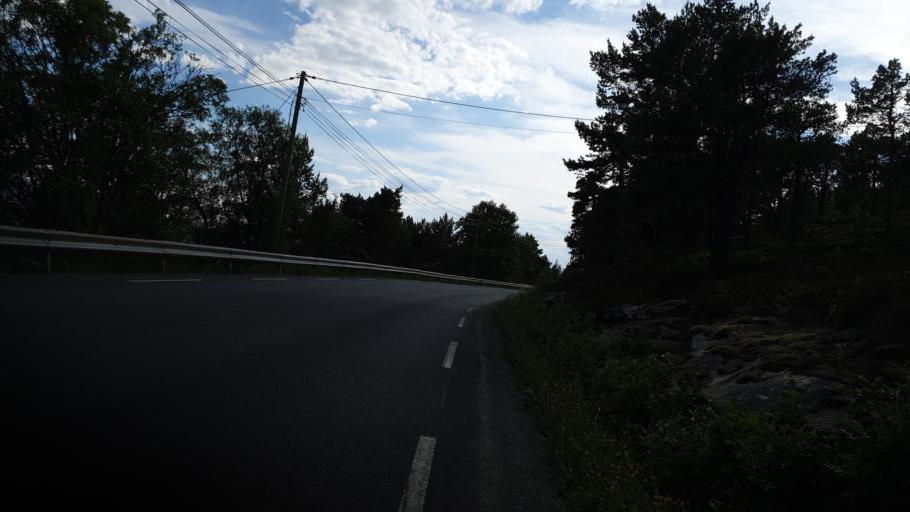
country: NO
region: Sor-Trondelag
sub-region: Trondheim
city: Trondheim
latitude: 63.5567
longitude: 10.3085
